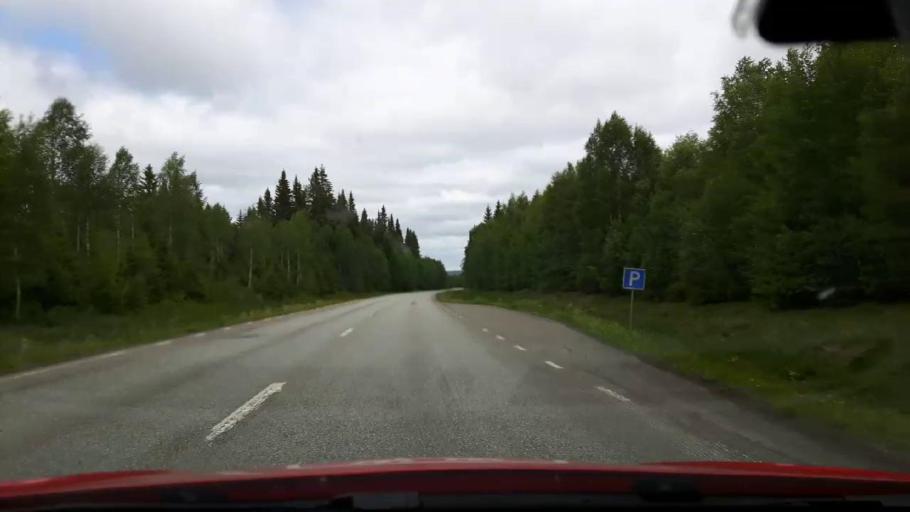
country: SE
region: Jaemtland
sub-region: Krokoms Kommun
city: Krokom
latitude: 63.3778
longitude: 14.5061
